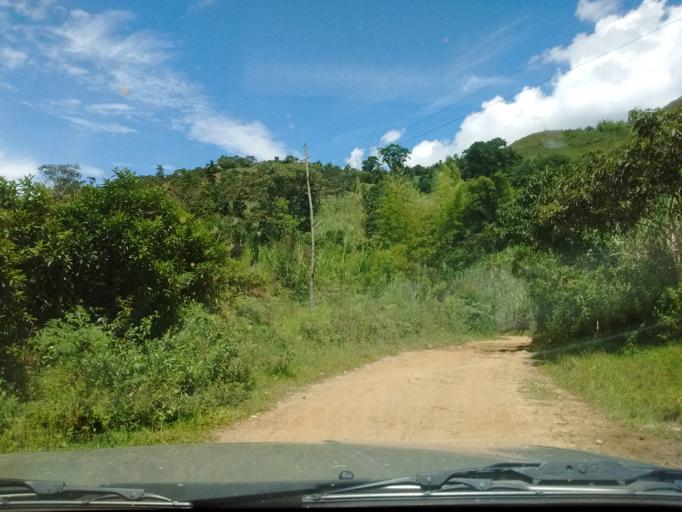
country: CO
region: Cauca
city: Villa Rica
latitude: 2.6357
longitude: -76.7711
